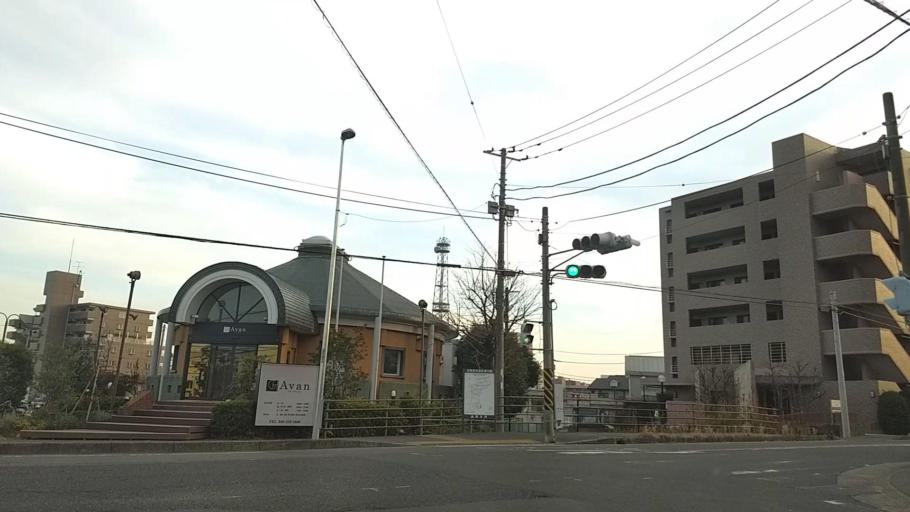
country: JP
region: Kanagawa
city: Atsugi
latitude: 35.4407
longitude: 139.3539
